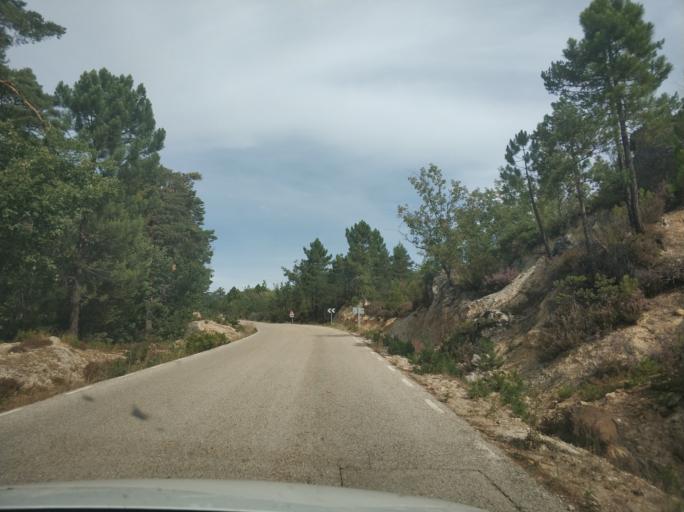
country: ES
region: Castille and Leon
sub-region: Provincia de Soria
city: Duruelo de la Sierra
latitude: 41.9100
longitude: -2.9470
